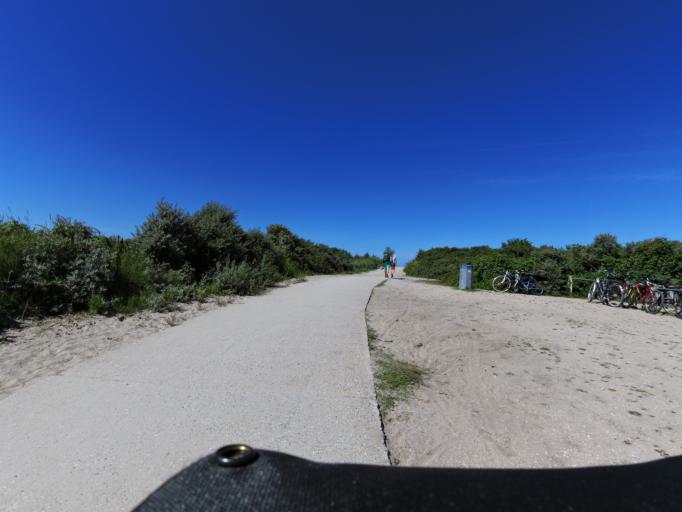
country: NL
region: Zeeland
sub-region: Schouwen-Duiveland
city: Haamstede
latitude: 51.7296
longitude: 3.7184
